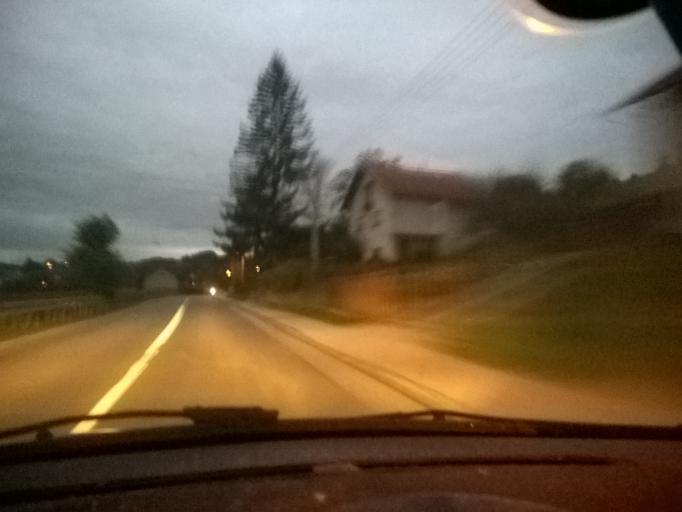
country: HR
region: Krapinsko-Zagorska
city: Zabok
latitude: 46.0336
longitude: 15.9278
